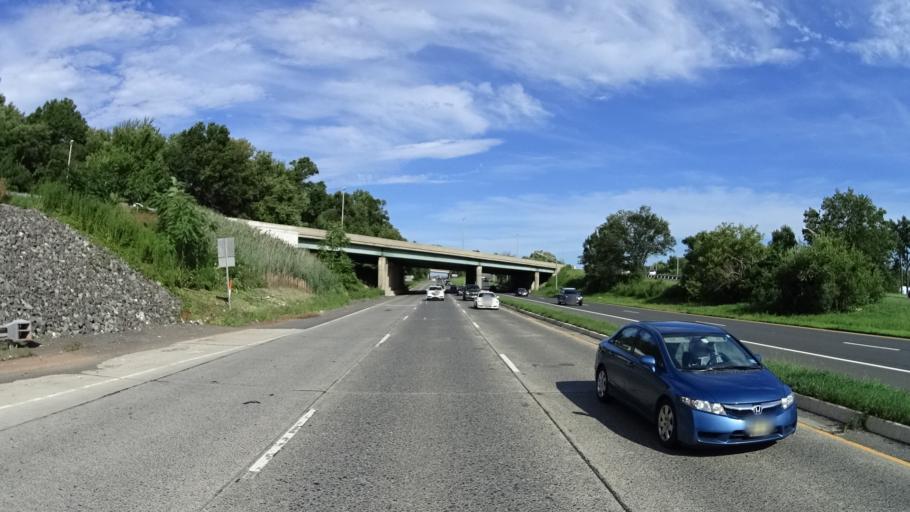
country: US
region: New Jersey
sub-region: Somerset County
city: Finderne
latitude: 40.5769
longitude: -74.5731
